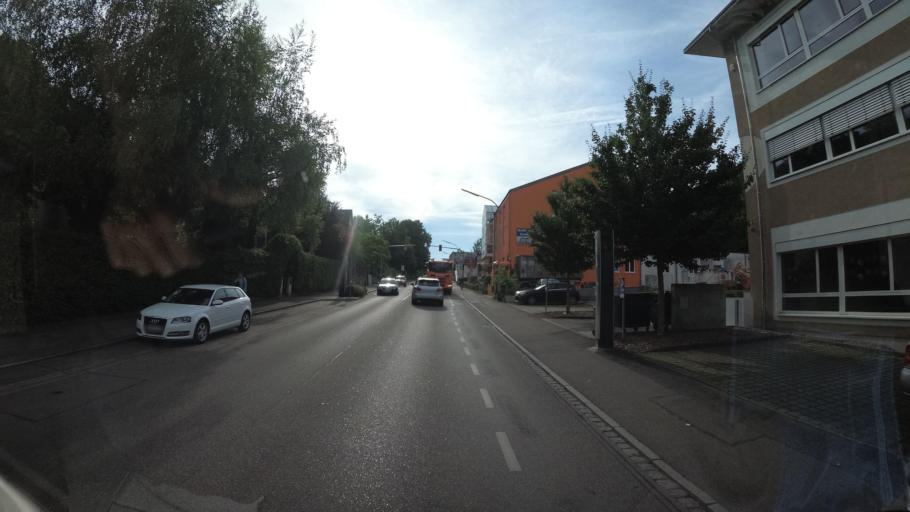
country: DE
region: Baden-Wuerttemberg
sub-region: Freiburg Region
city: Loerrach
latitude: 47.6099
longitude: 7.6688
